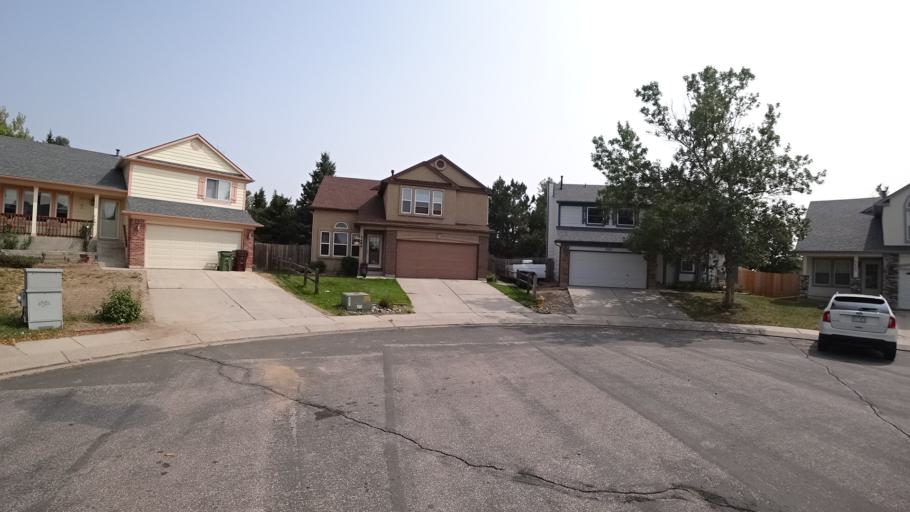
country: US
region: Colorado
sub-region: El Paso County
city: Cimarron Hills
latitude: 38.9209
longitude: -104.7228
